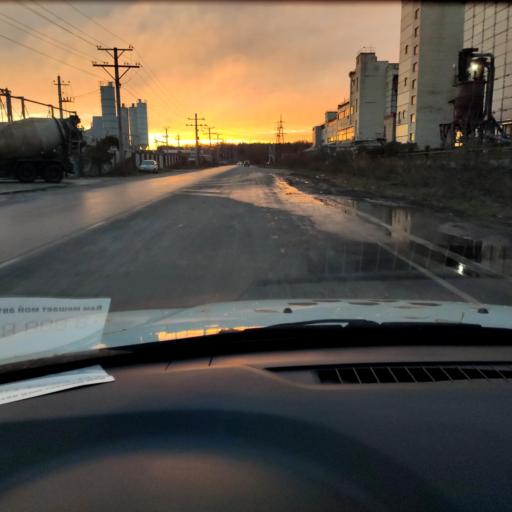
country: RU
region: Samara
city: Zhigulevsk
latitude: 53.5252
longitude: 49.4850
